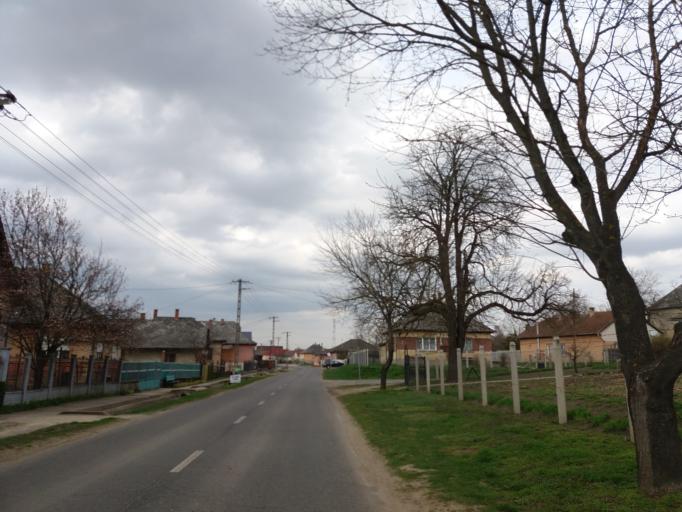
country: HU
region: Szabolcs-Szatmar-Bereg
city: Nyirtass
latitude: 48.1149
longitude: 22.0217
